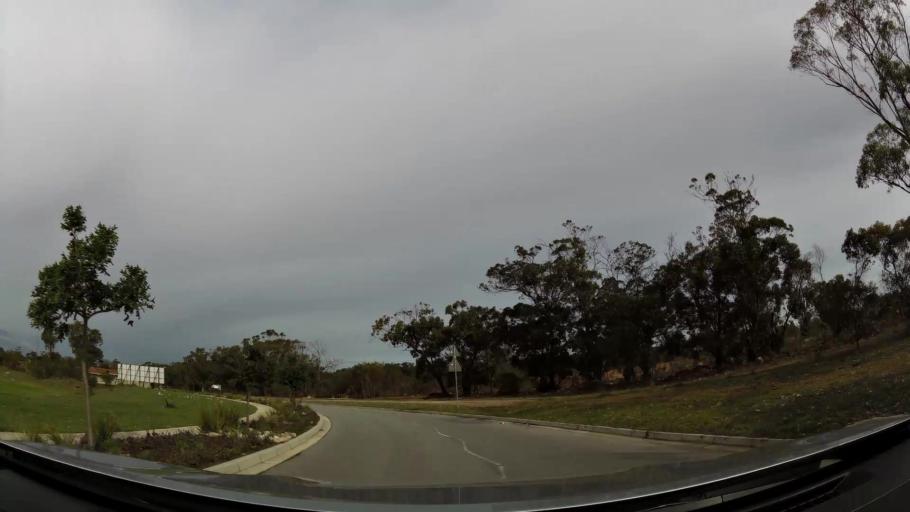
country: ZA
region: Eastern Cape
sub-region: Nelson Mandela Bay Metropolitan Municipality
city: Port Elizabeth
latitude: -33.9338
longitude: 25.4901
